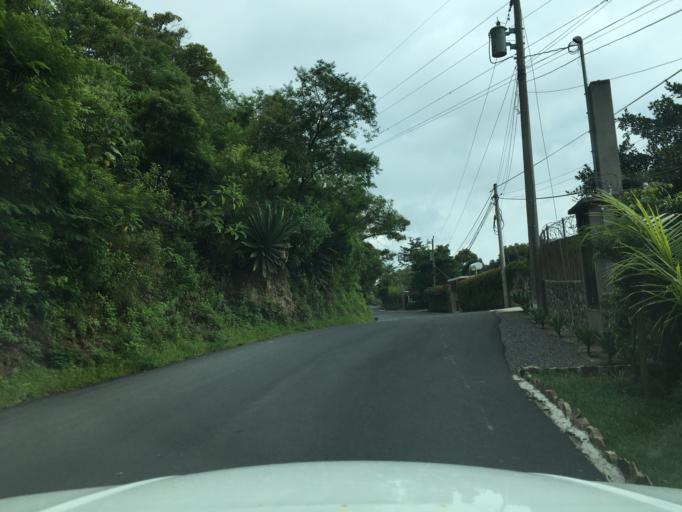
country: GT
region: Solola
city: Panajachel
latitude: 14.7296
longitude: -91.1415
